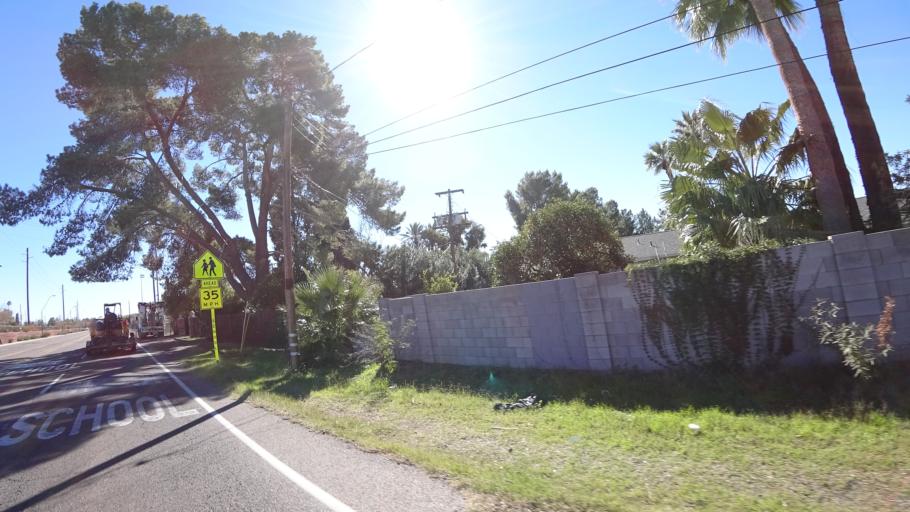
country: US
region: Arizona
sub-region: Maricopa County
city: Paradise Valley
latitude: 33.4908
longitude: -111.9670
